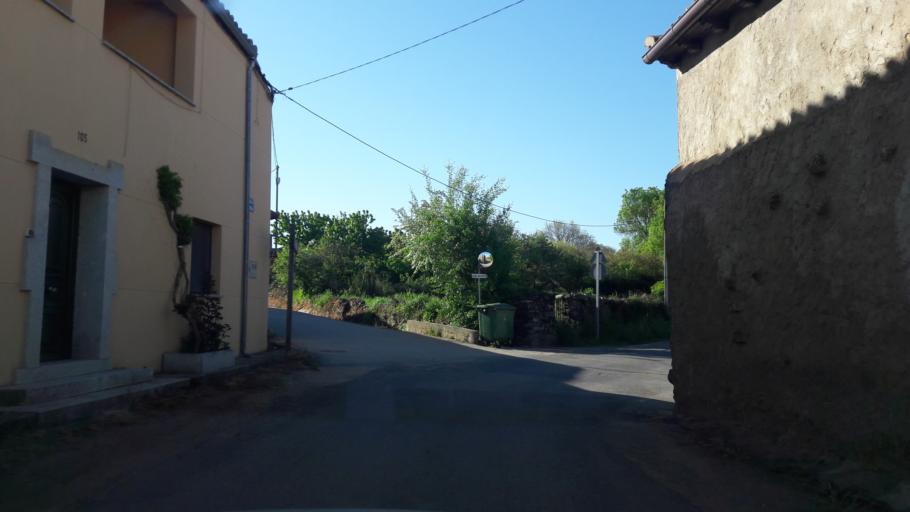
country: ES
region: Castille and Leon
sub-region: Provincia de Salamanca
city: Endrinal
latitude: 40.5890
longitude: -5.8034
